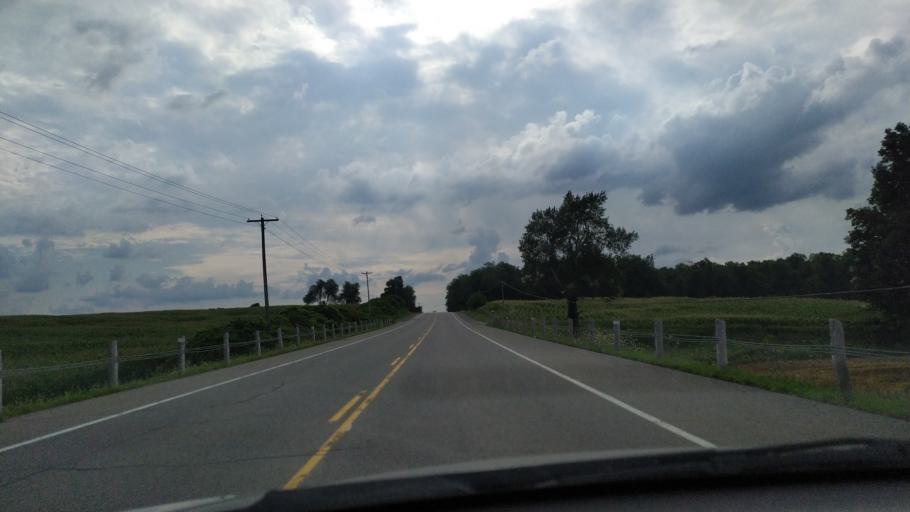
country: CA
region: Ontario
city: Kitchener
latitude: 43.3566
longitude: -80.4895
